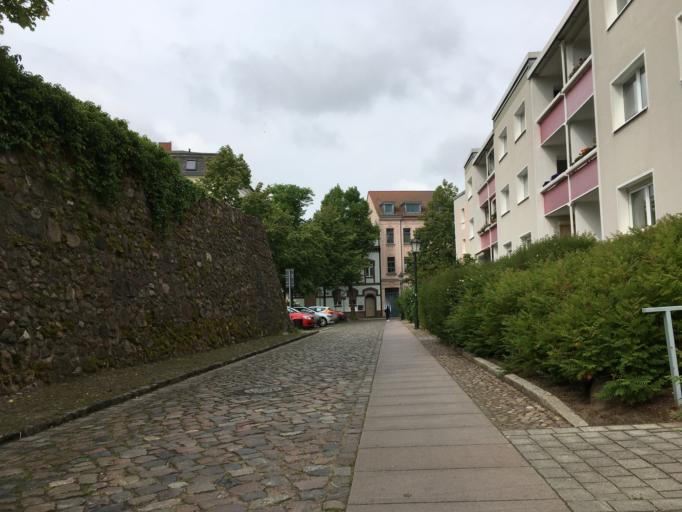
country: DE
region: Brandenburg
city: Bernau bei Berlin
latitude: 52.6768
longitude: 13.5873
